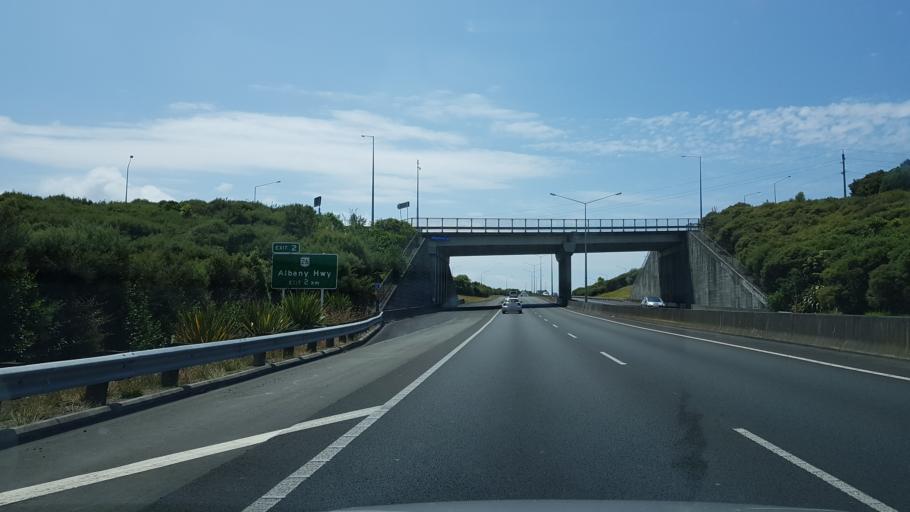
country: NZ
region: Auckland
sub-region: Auckland
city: North Shore
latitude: -36.7729
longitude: 174.6852
